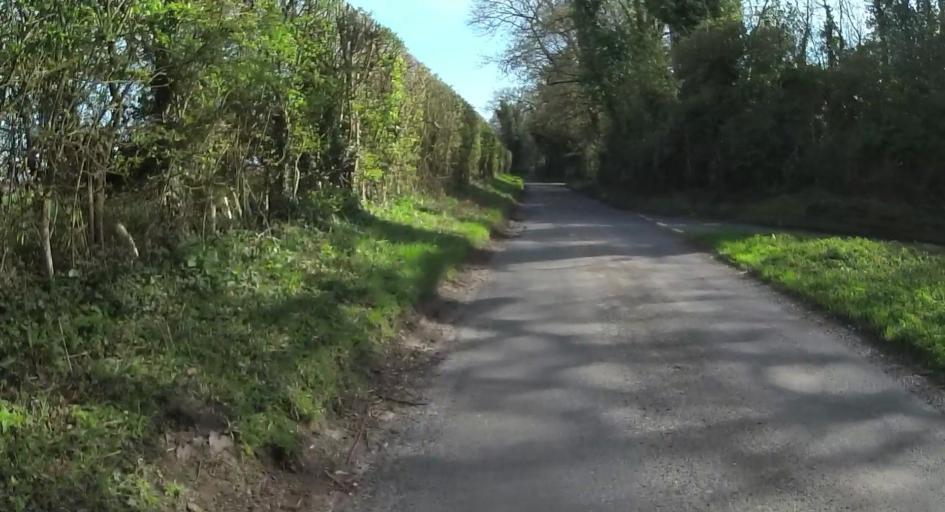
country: GB
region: England
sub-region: Hampshire
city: Highclere
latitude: 51.2633
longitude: -1.3698
